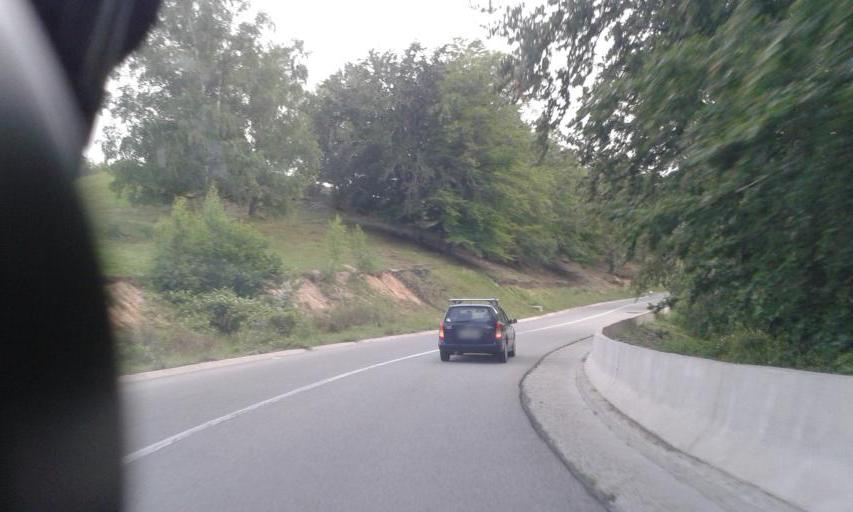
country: RO
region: Gorj
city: Novaci-Straini
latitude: 45.2050
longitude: 23.6982
